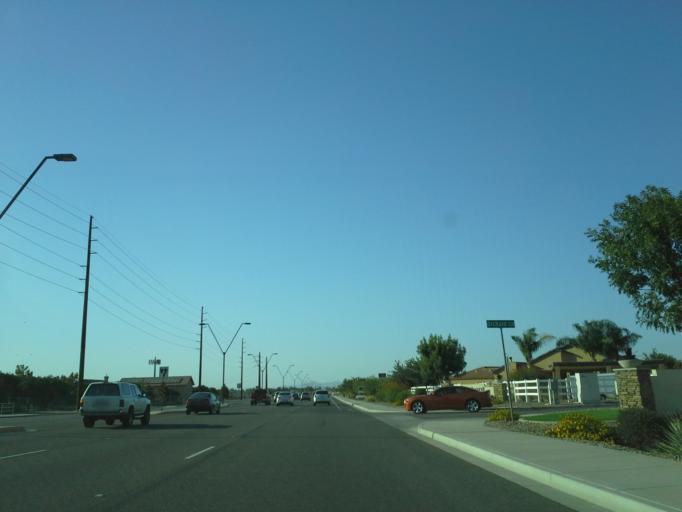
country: US
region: Arizona
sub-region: Maricopa County
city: Queen Creek
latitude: 33.2134
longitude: -111.6344
